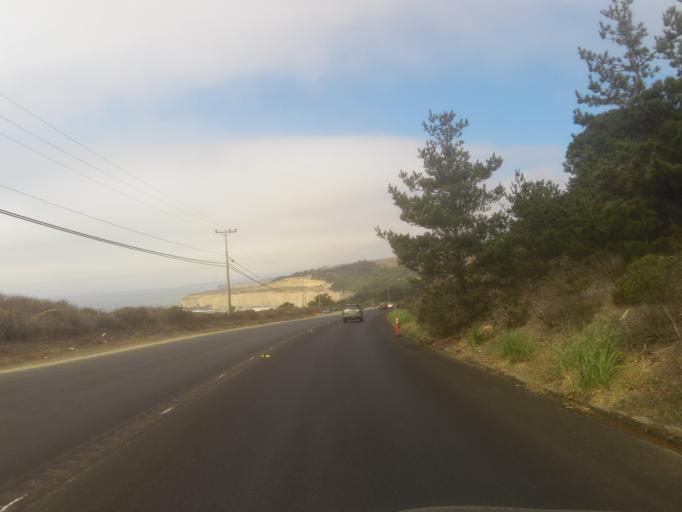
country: US
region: California
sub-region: San Mateo County
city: Half Moon Bay
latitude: 37.3509
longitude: -122.3985
